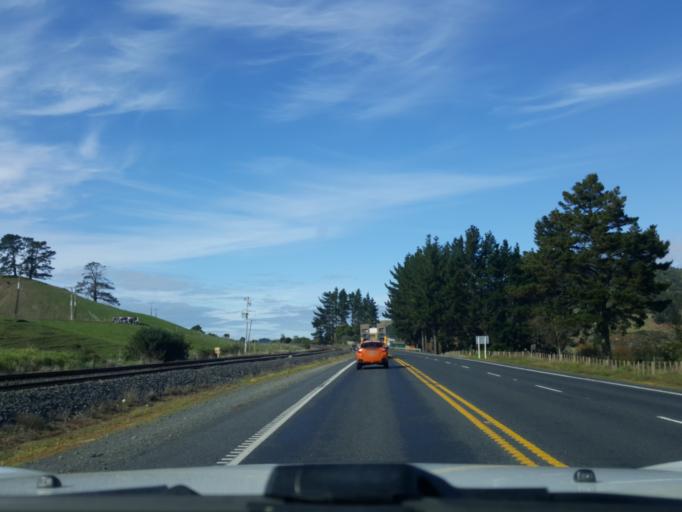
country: NZ
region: Waikato
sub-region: Waikato District
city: Ngaruawahia
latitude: -37.5971
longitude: 175.1627
